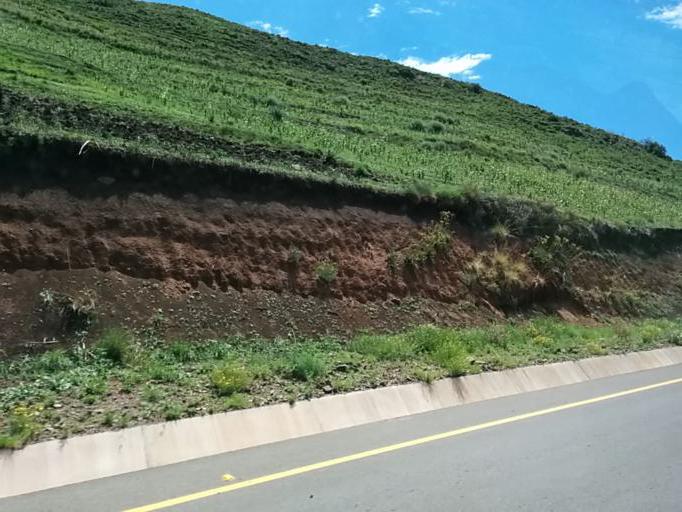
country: LS
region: Maseru
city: Nako
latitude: -29.9297
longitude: 28.1583
